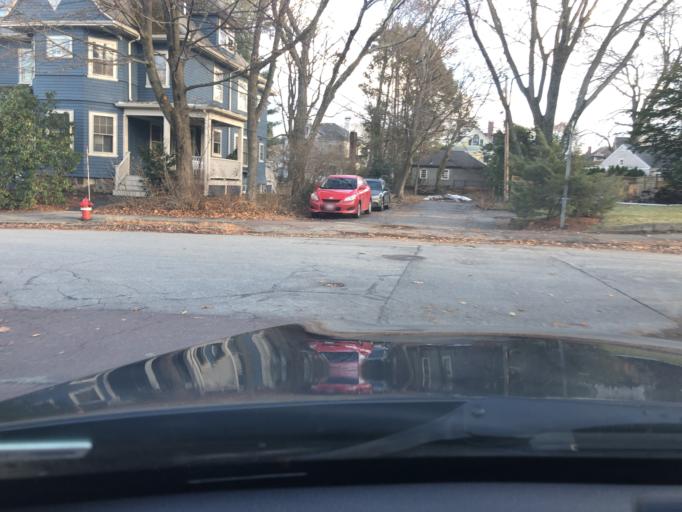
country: US
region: Massachusetts
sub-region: Middlesex County
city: Arlington
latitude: 42.4143
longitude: -71.1616
